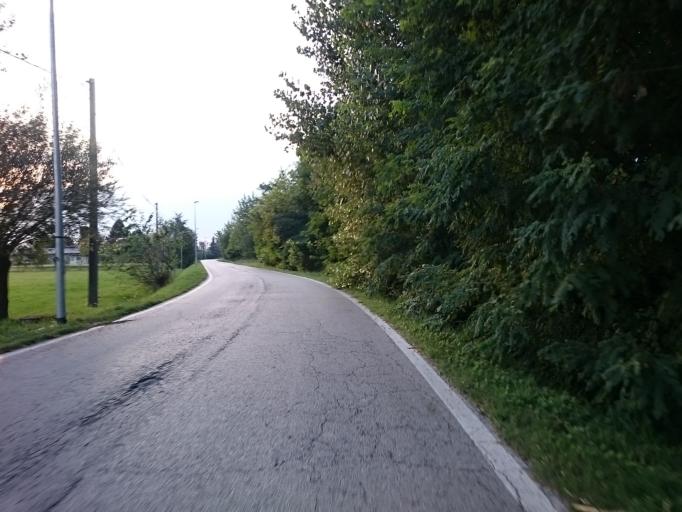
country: IT
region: Veneto
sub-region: Provincia di Vicenza
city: Grisignano di Zocco
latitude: 45.4893
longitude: 11.7182
